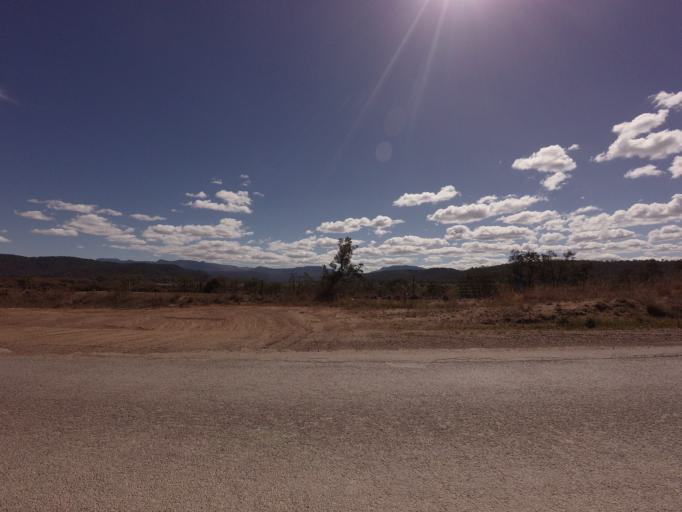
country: AU
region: Tasmania
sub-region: Break O'Day
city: St Helens
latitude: -41.6478
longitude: 147.9357
